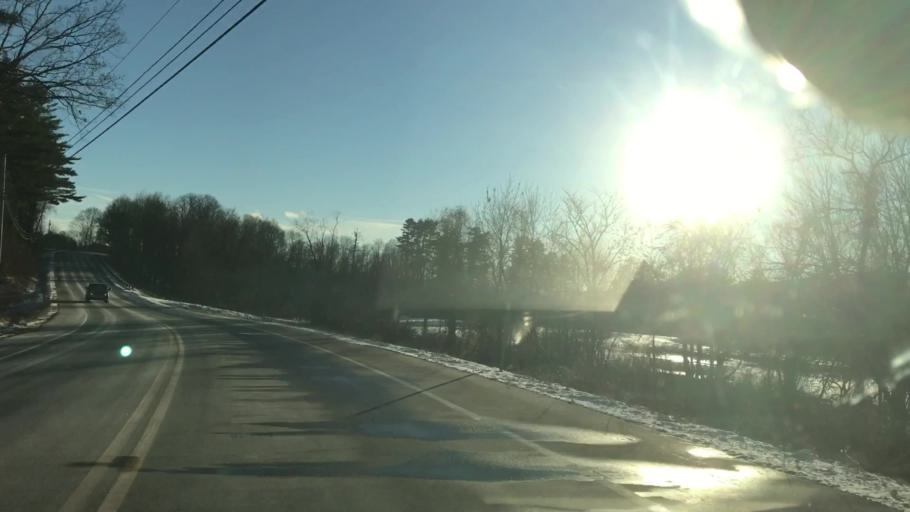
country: US
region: New Hampshire
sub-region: Grafton County
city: Orford
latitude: 43.8903
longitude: -72.1504
